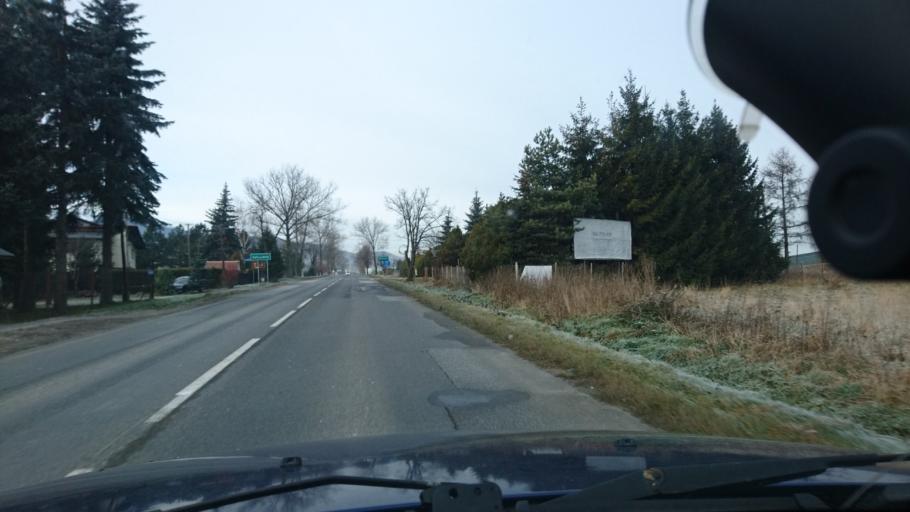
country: PL
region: Silesian Voivodeship
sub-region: Powiat bielski
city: Rybarzowice
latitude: 49.7345
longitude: 19.1131
